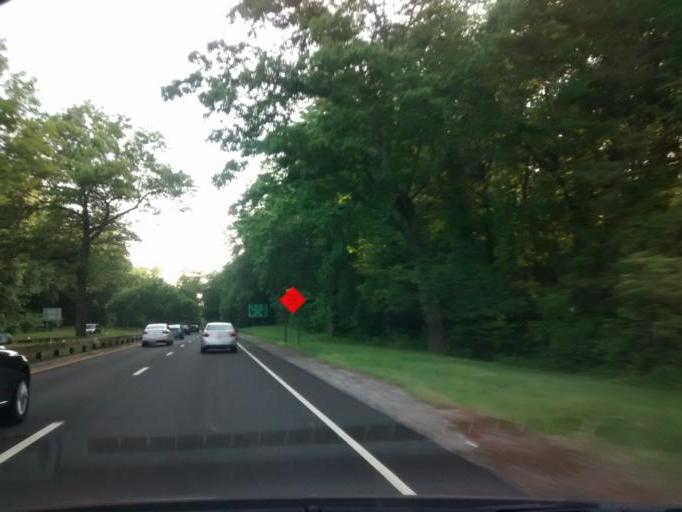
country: US
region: Connecticut
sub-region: Fairfield County
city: Glenville
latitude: 41.0918
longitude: -73.6568
